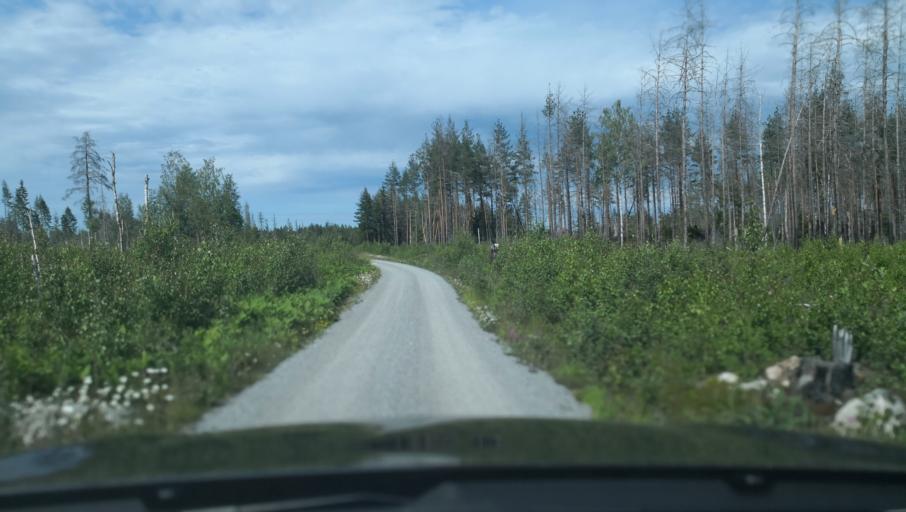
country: SE
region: Vaestmanland
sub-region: Surahammars Kommun
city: Ramnas
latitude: 59.9349
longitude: 16.1928
